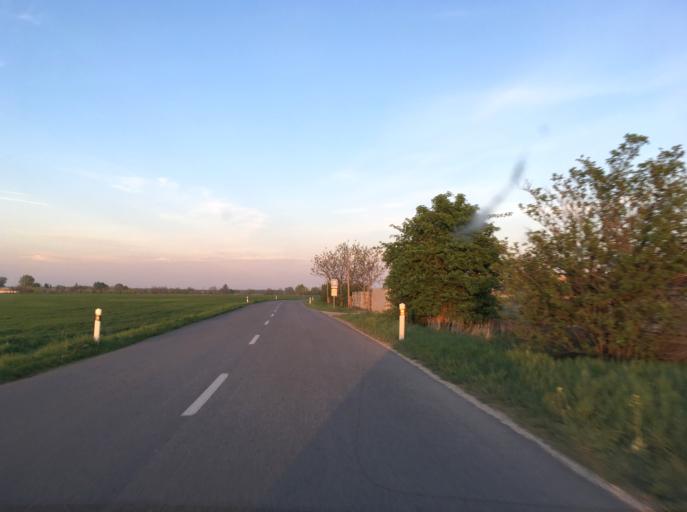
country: SK
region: Nitriansky
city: Kolarovo
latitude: 47.9002
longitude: 17.9630
